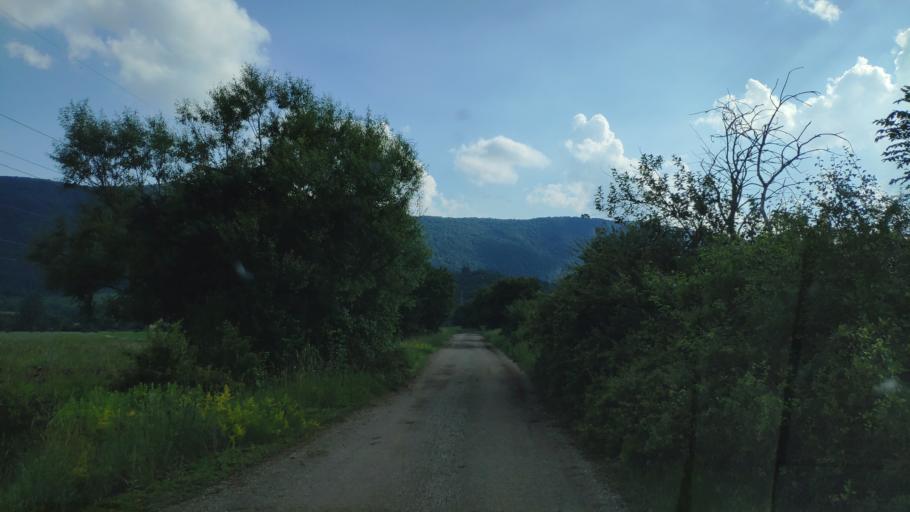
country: SK
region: Kosicky
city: Medzev
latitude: 48.5953
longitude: 20.7316
